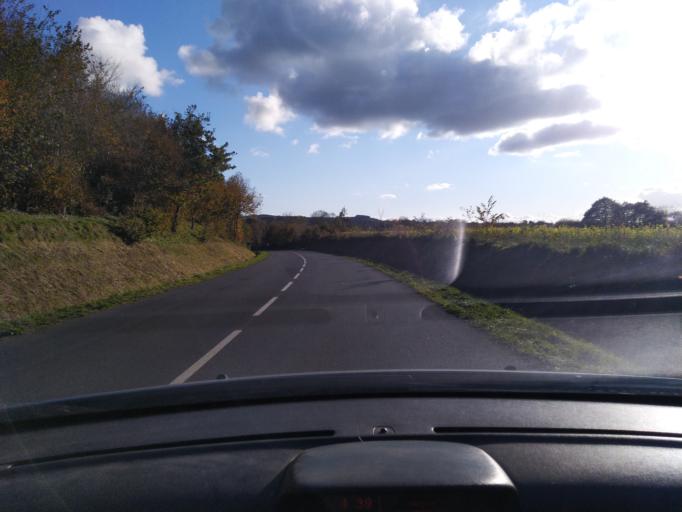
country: FR
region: Brittany
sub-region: Departement des Cotes-d'Armor
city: Plestin-les-Greves
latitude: 48.5923
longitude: -3.6071
